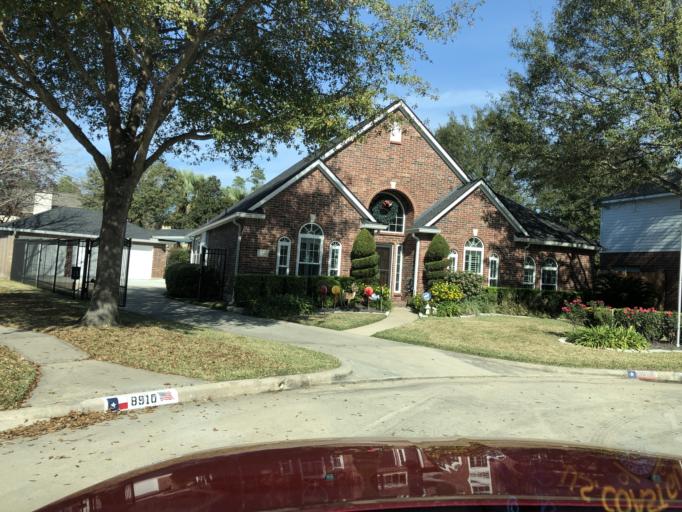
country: US
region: Texas
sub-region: Harris County
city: Tomball
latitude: 30.0227
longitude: -95.5568
